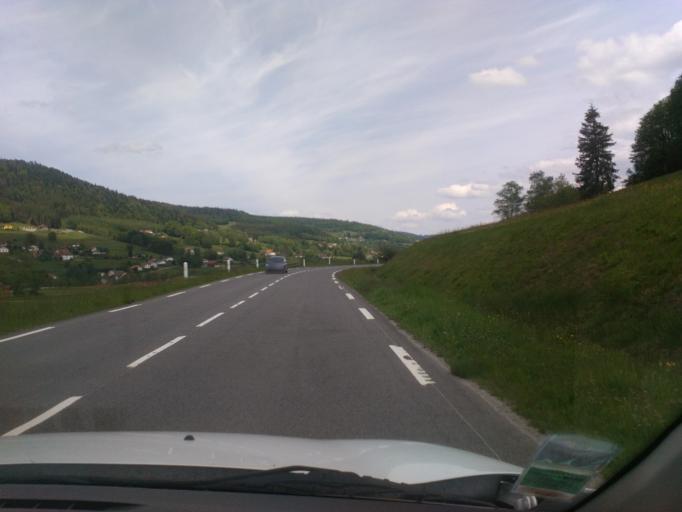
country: FR
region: Lorraine
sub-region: Departement des Vosges
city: Le Syndicat
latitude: 48.0527
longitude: 6.6974
